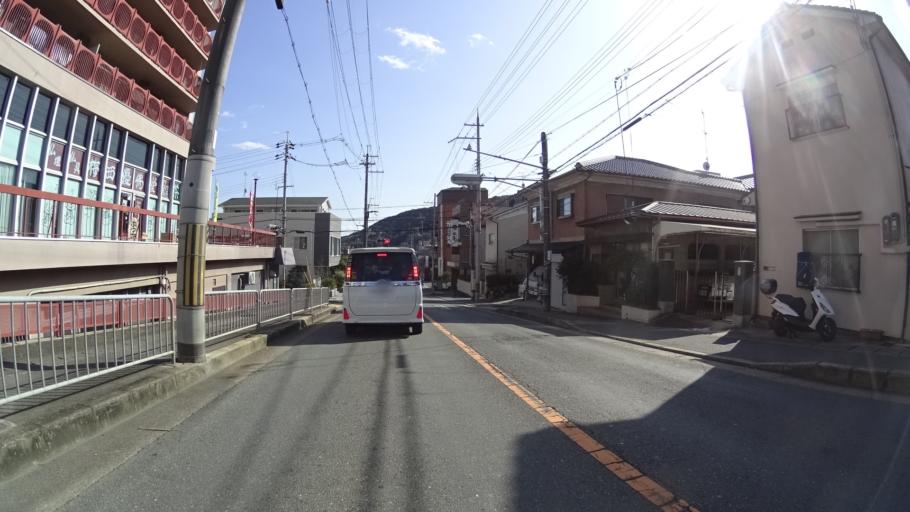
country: JP
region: Kyoto
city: Kyoto
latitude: 34.9803
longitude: 135.7957
